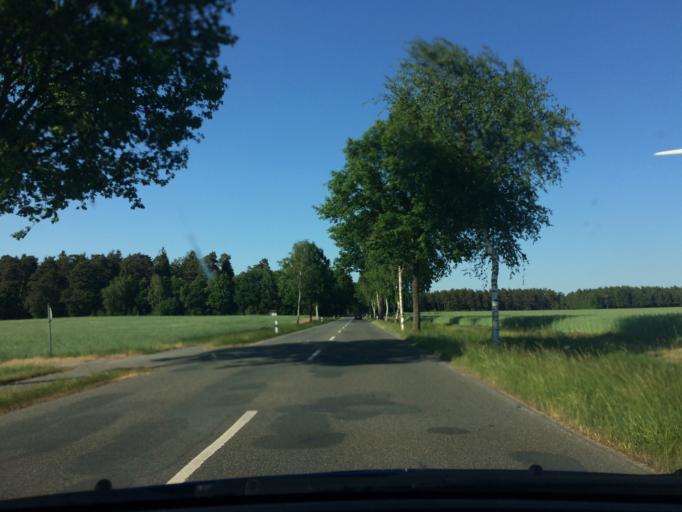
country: DE
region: Lower Saxony
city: Bispingen
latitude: 53.0435
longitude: 9.9346
